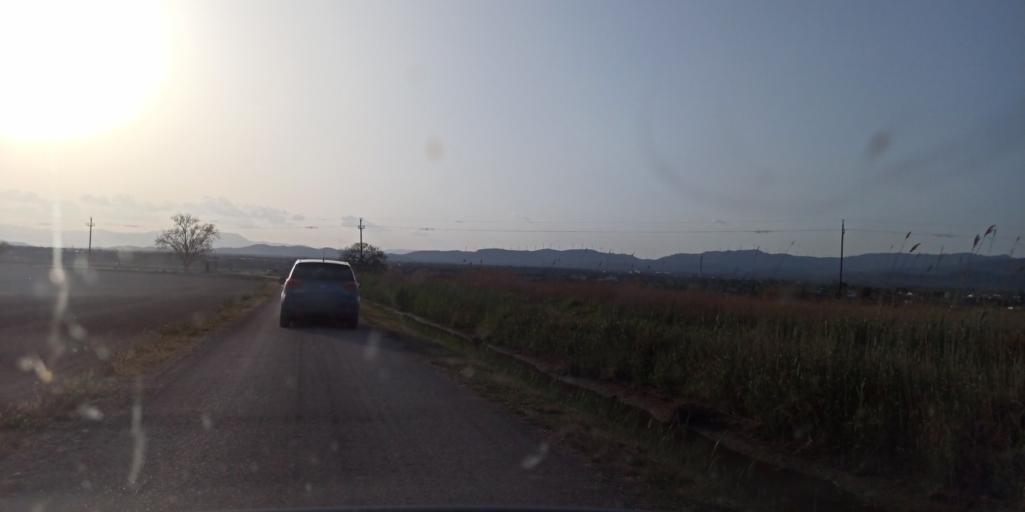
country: ES
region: Catalonia
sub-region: Provincia de Tarragona
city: L'Ampolla
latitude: 40.7849
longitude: 0.6990
